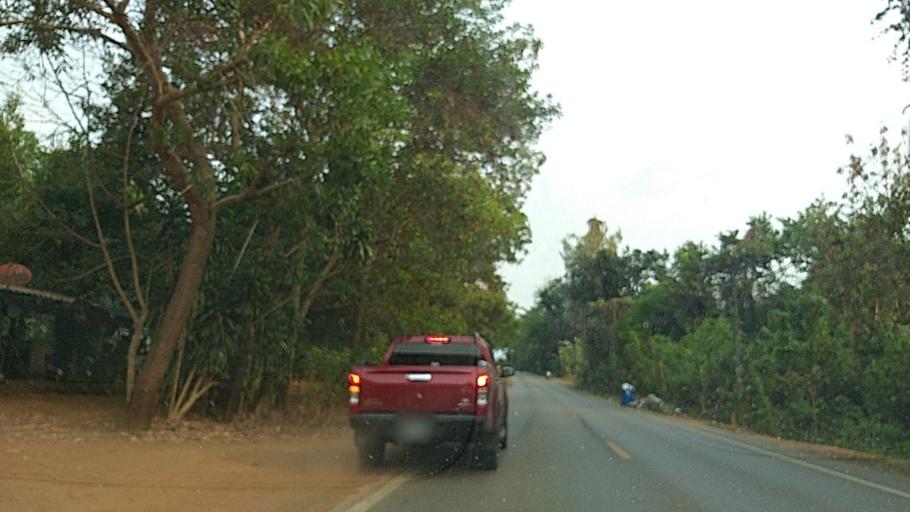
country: TH
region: Trat
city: Laem Ngop
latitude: 12.1960
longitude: 102.2883
